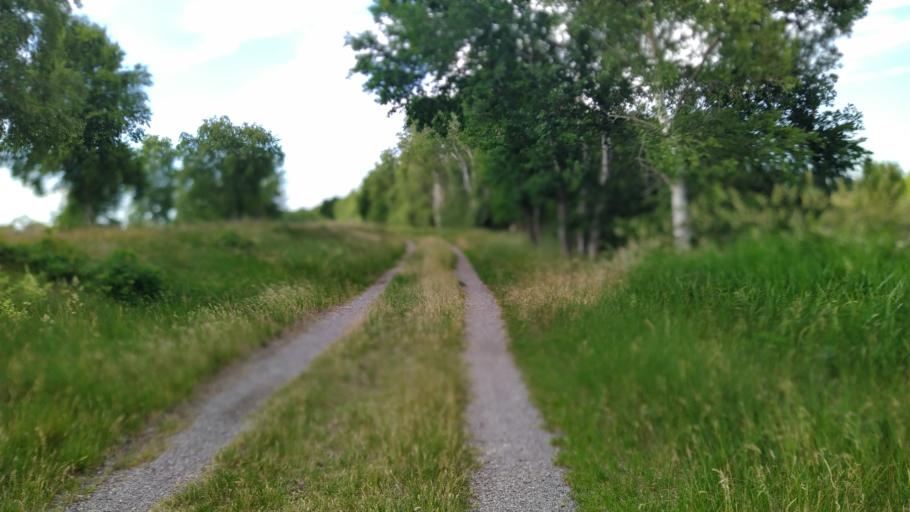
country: DE
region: Lower Saxony
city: Stinstedt
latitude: 53.6461
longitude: 8.9488
